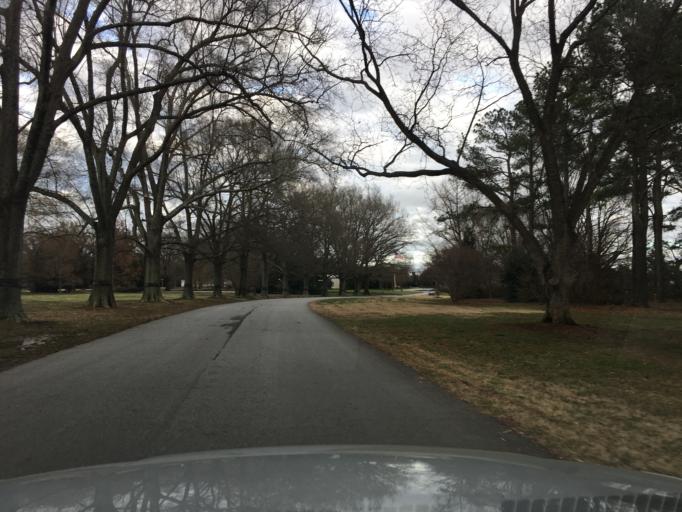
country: US
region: South Carolina
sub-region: Spartanburg County
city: Saxon
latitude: 34.9897
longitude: -81.9608
